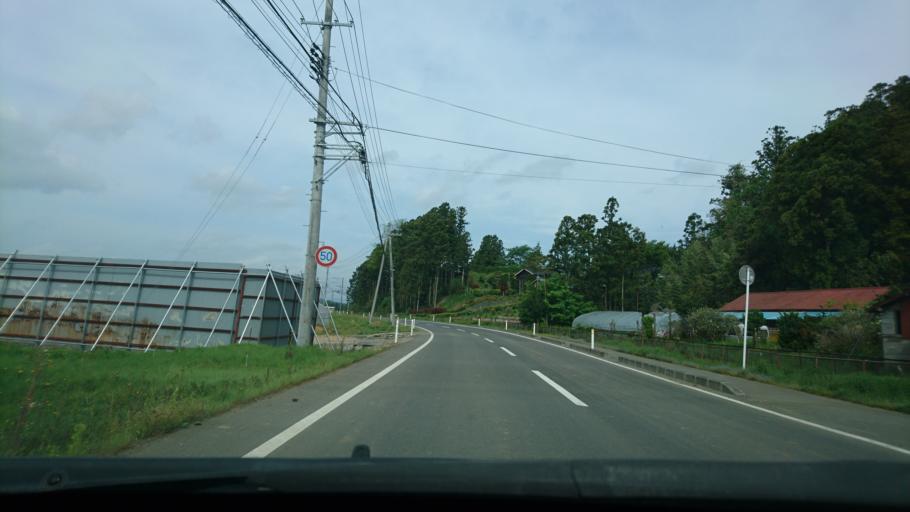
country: JP
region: Iwate
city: Ichinoseki
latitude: 38.8156
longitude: 141.0536
